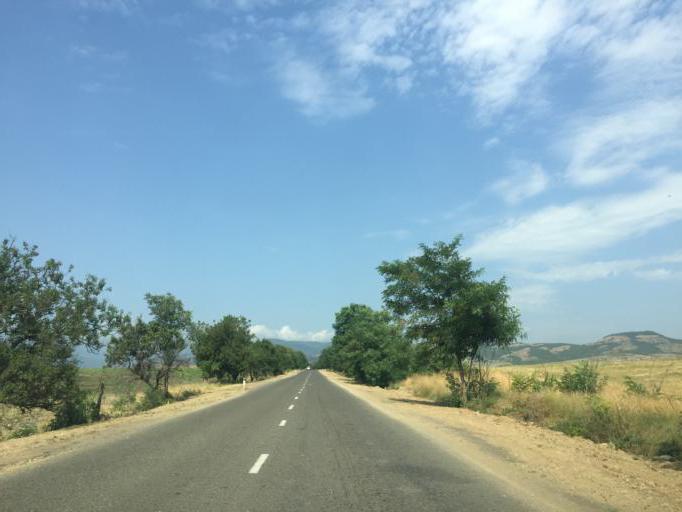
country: AZ
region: Xocali
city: Xocali
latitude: 39.8714
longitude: 46.7659
